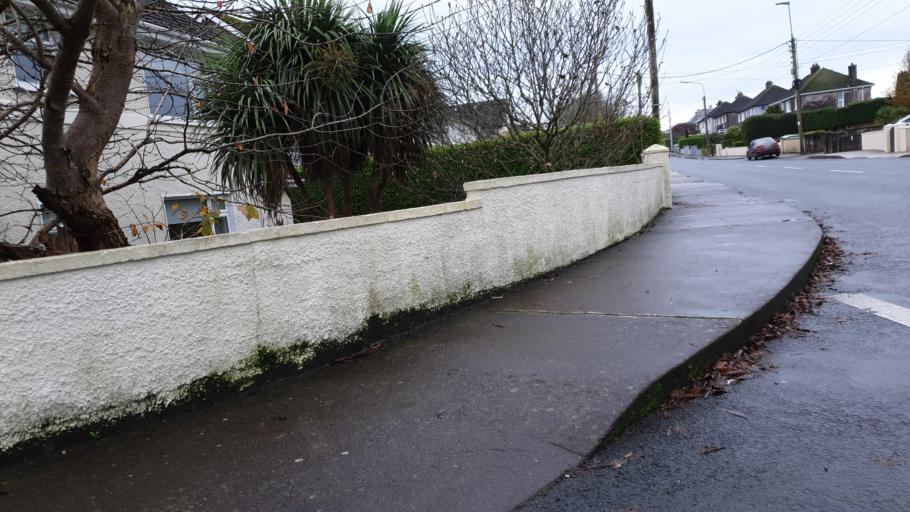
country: IE
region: Munster
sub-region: County Cork
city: Cork
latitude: 51.8913
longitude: -8.4219
